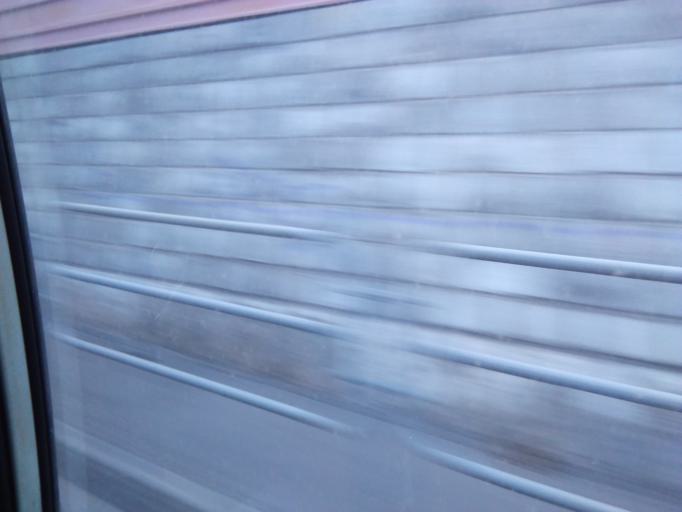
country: RU
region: Chelyabinsk
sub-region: Gorod Magnitogorsk
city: Magnitogorsk
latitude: 53.3881
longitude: 59.0528
